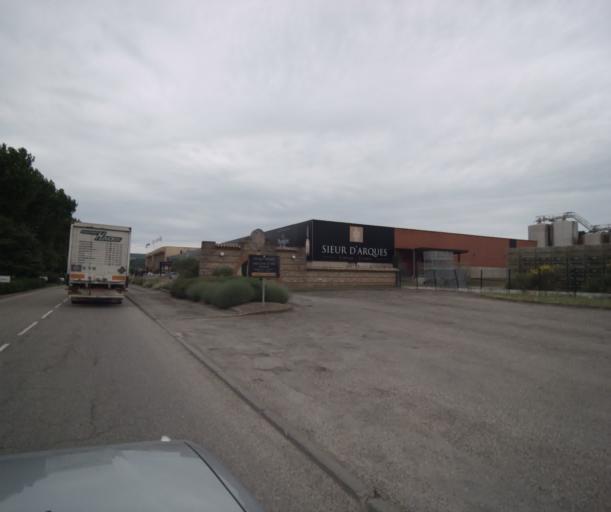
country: FR
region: Languedoc-Roussillon
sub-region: Departement de l'Aude
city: Limoux
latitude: 43.0728
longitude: 2.2200
